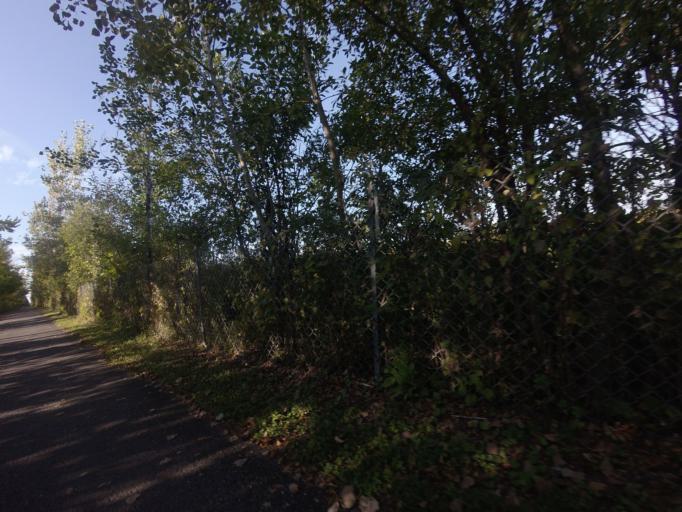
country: CA
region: Quebec
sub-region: Laurentides
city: Blainville
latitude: 45.7268
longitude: -73.9384
